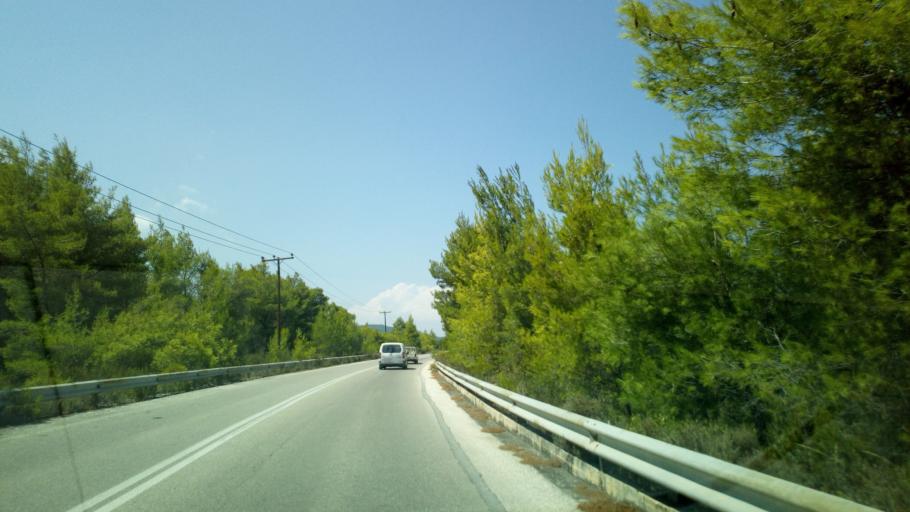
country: GR
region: Central Macedonia
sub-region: Nomos Chalkidikis
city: Sarti
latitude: 40.1264
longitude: 23.9459
